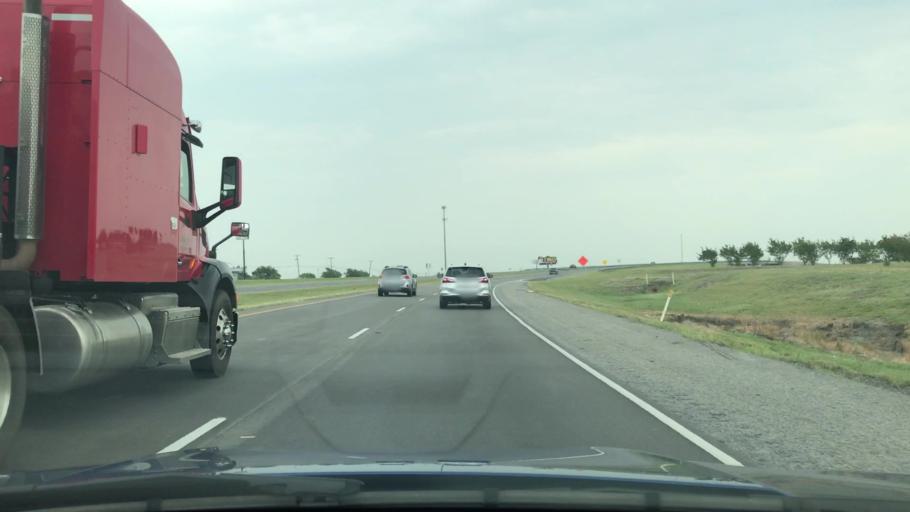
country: US
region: Texas
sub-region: Kaufman County
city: Talty
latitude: 32.7401
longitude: -96.3633
